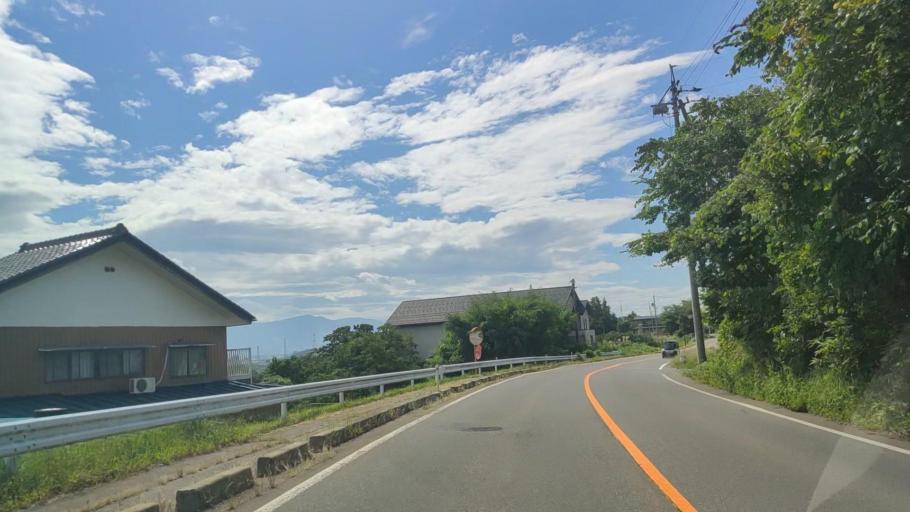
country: JP
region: Nagano
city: Nakano
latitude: 36.7490
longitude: 138.3148
